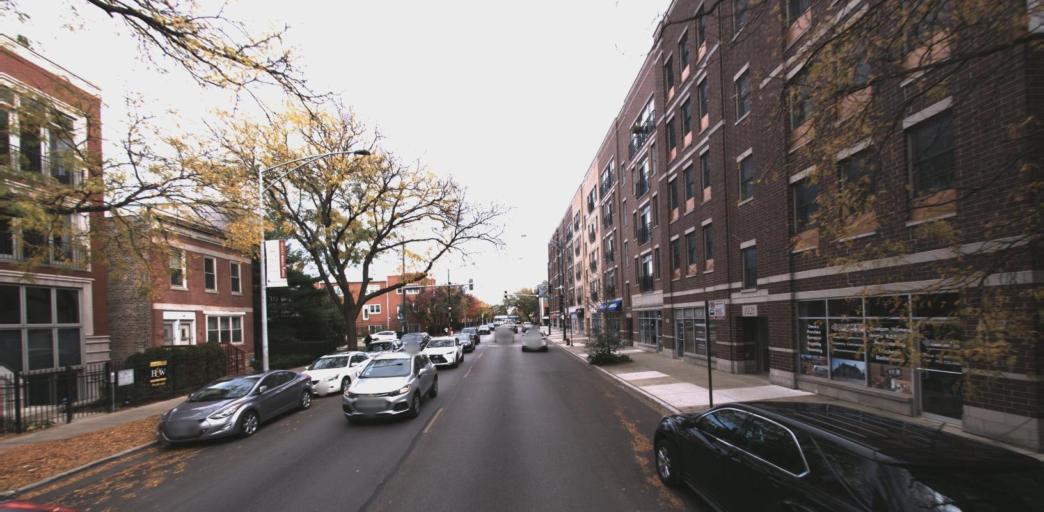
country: US
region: Illinois
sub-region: Cook County
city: Chicago
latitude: 41.9323
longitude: -87.6762
